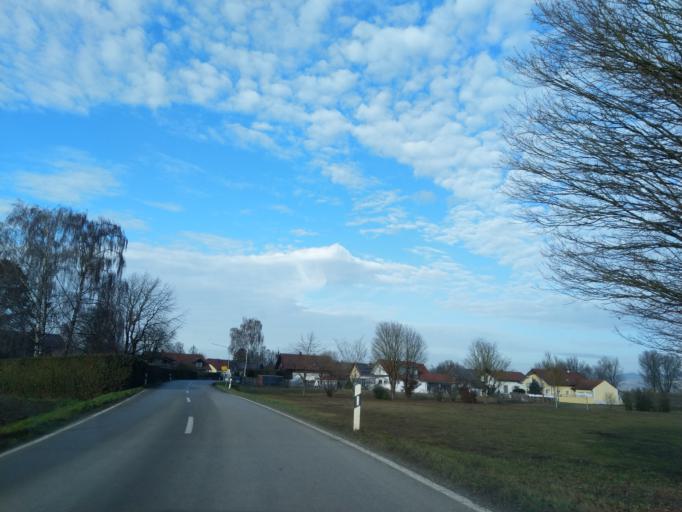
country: DE
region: Bavaria
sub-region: Lower Bavaria
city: Niederalteich
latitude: 48.7540
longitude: 13.0234
